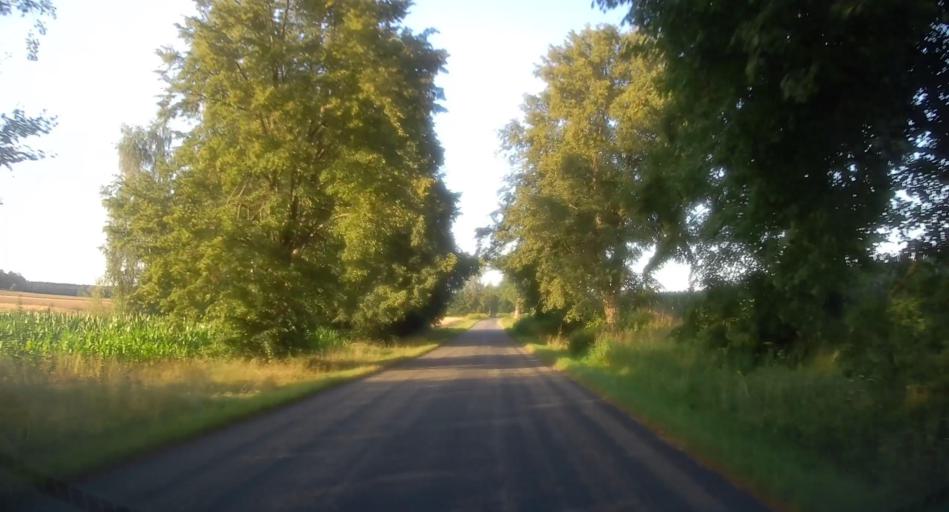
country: PL
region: Lodz Voivodeship
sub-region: Powiat skierniewicki
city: Kaweczyn Nowy
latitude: 51.8860
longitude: 20.2833
